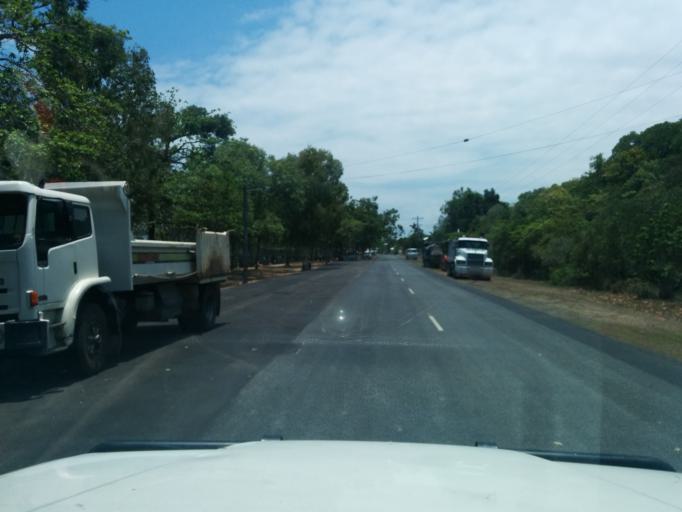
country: AU
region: Queensland
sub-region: Cairns
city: Yorkeys Knob
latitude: -16.8339
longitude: 145.7374
